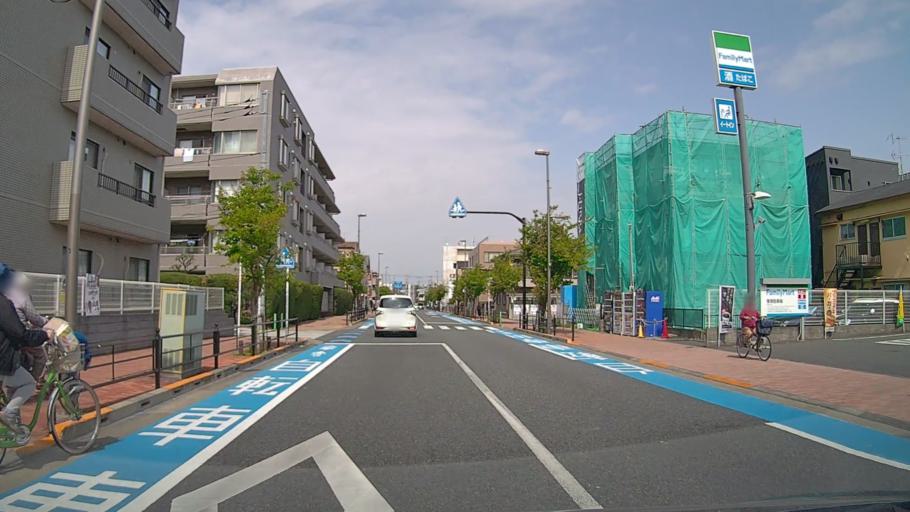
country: JP
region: Saitama
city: Wako
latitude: 35.7484
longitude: 139.6078
